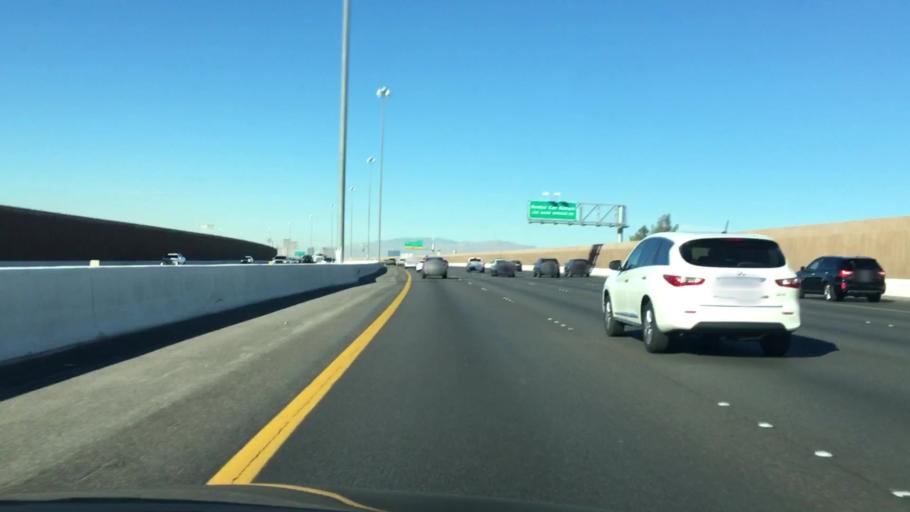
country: US
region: Nevada
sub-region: Clark County
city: Paradise
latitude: 36.0463
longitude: -115.1343
